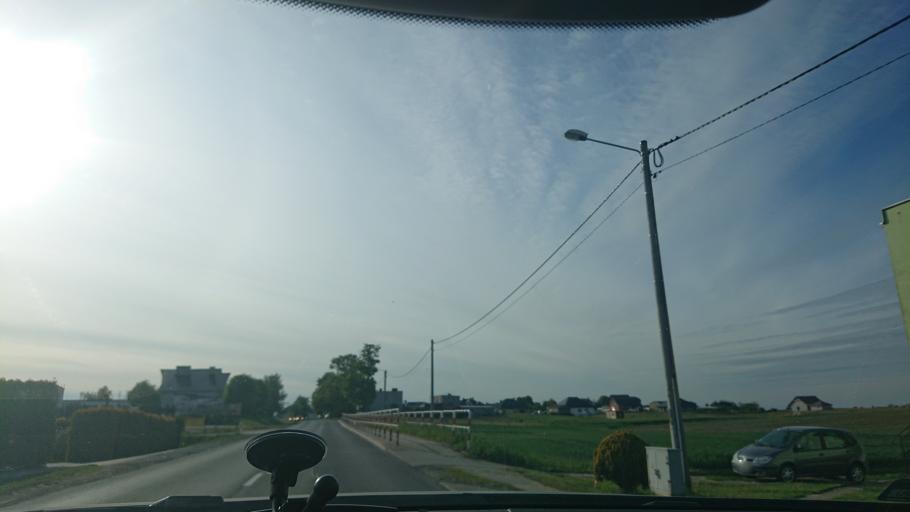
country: PL
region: Greater Poland Voivodeship
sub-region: Powiat gnieznienski
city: Gniezno
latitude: 52.5489
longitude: 17.5579
